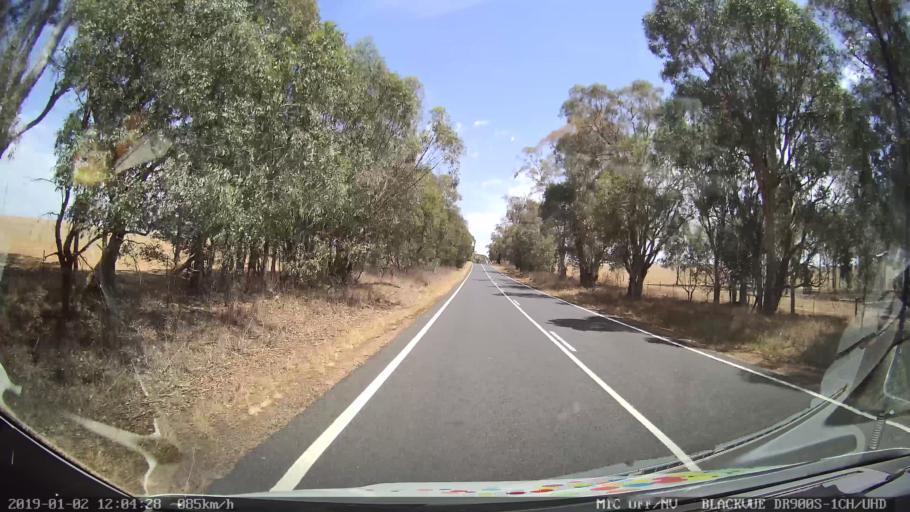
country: AU
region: New South Wales
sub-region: Young
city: Young
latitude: -34.5241
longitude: 148.3103
